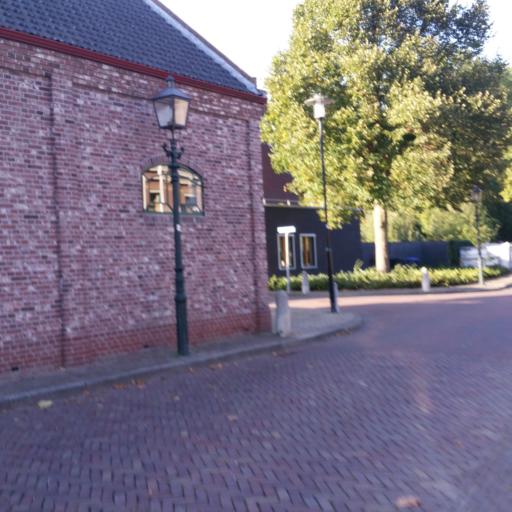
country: NL
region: Utrecht
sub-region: Gemeente Lopik
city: Lopik
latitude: 51.9697
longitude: 4.9769
